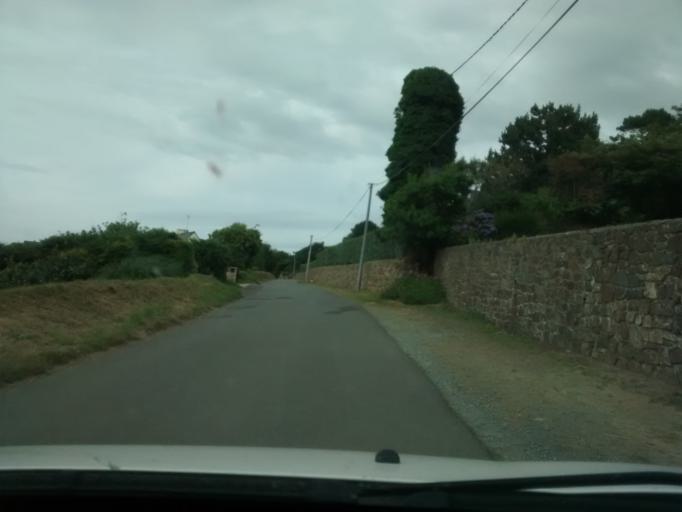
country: FR
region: Brittany
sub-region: Departement des Cotes-d'Armor
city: Plougrescant
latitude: 48.8392
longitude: -3.2509
